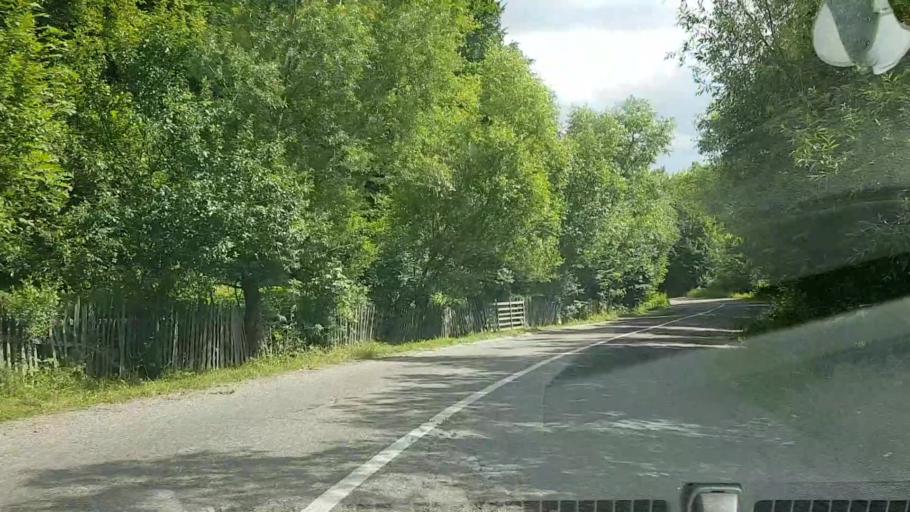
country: RO
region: Neamt
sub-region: Comuna Ceahlau
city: Ceahlau
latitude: 47.0589
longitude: 25.9697
